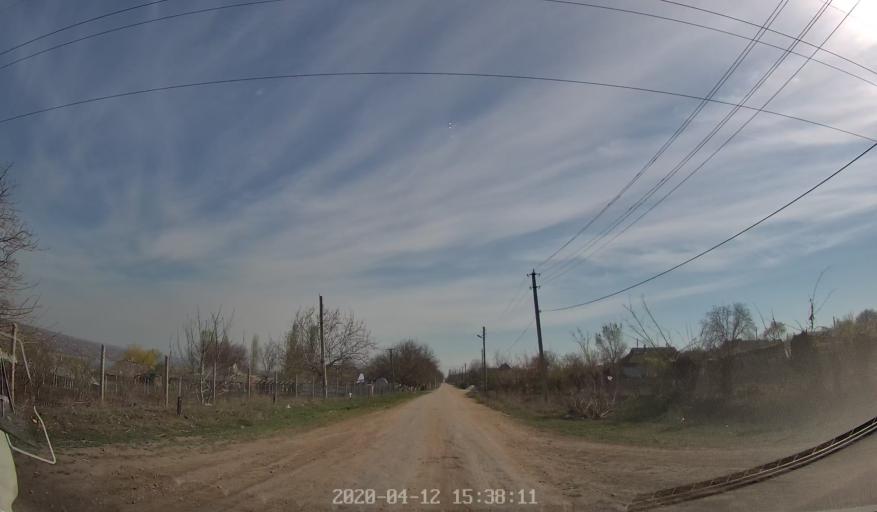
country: MD
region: Telenesti
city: Cocieri
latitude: 47.3196
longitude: 29.0689
